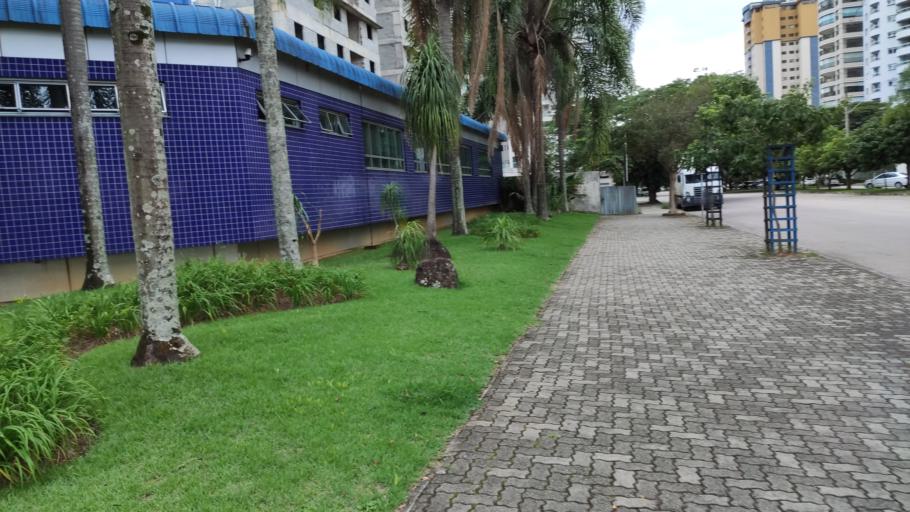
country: BR
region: Sao Paulo
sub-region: Sao Jose Dos Campos
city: Sao Jose dos Campos
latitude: -23.2173
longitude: -45.9094
